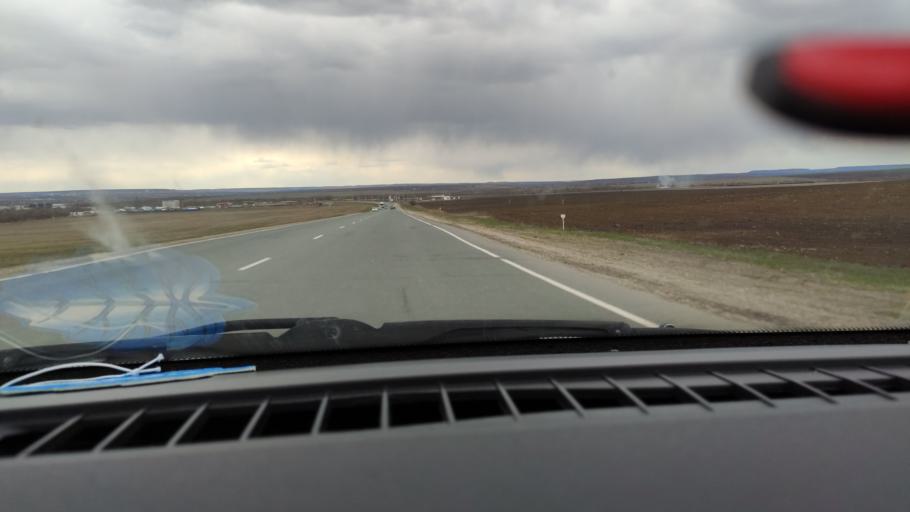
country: RU
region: Saratov
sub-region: Saratovskiy Rayon
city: Saratov
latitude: 51.7385
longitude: 46.0412
